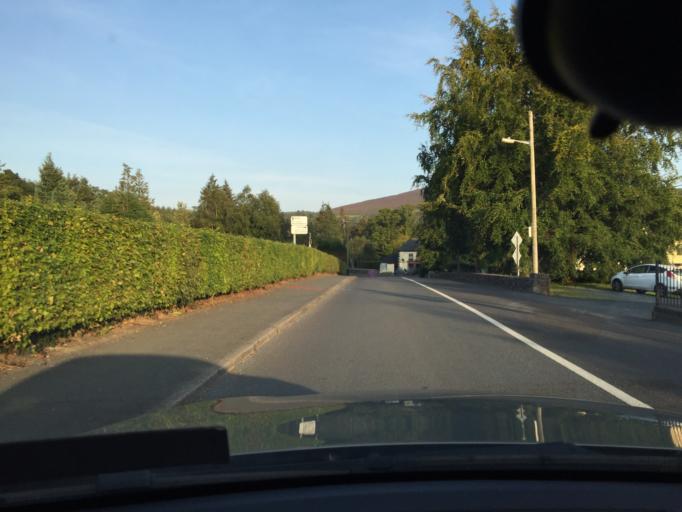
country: IE
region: Leinster
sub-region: Wicklow
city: Rathdrum
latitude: 53.0088
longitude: -6.2991
